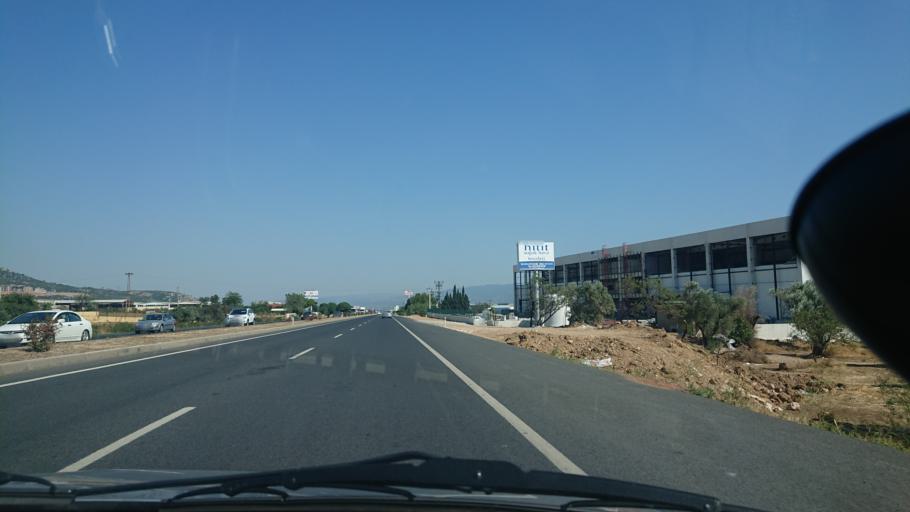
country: TR
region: Izmir
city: Kemalpasa
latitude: 38.4525
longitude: 27.4692
